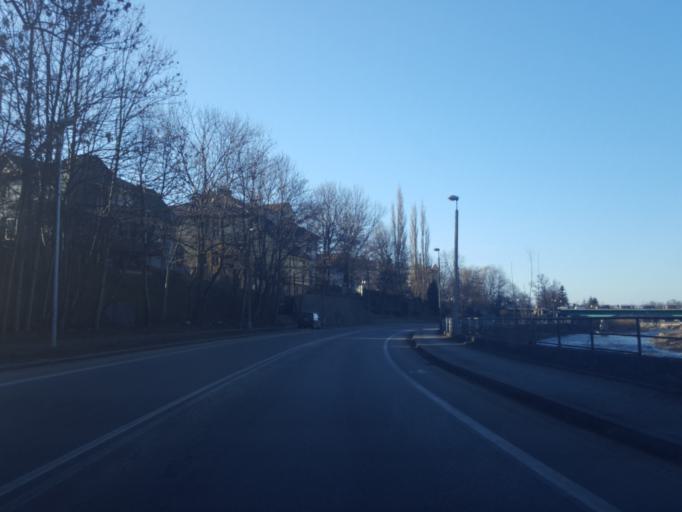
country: PL
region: Lesser Poland Voivodeship
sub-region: Powiat nowosadecki
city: Nowy Sacz
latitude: 49.6226
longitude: 20.6969
